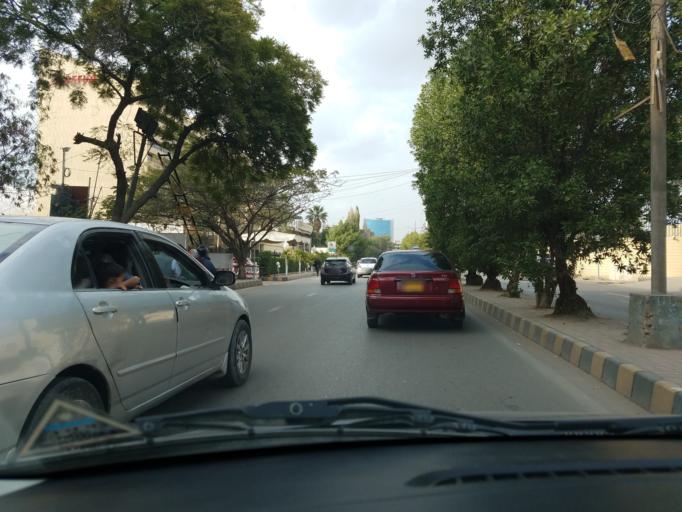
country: PK
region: Sindh
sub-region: Karachi District
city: Karachi
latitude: 24.8452
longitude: 67.0319
